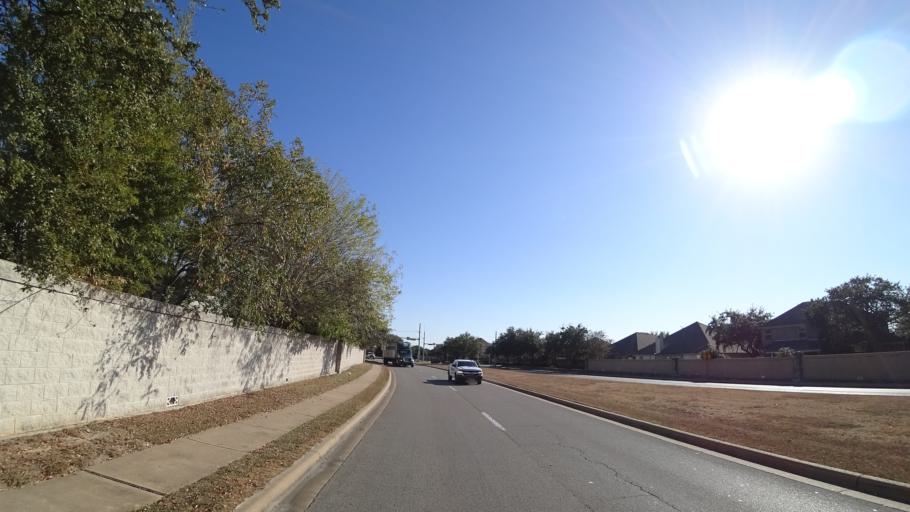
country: US
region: Texas
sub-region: Williamson County
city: Anderson Mill
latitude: 30.4636
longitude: -97.8436
